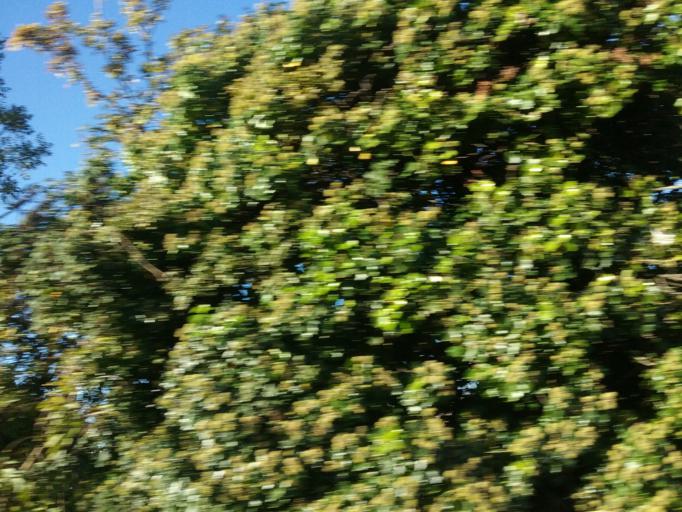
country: IE
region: Leinster
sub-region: Lu
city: Drogheda
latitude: 53.7150
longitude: -6.3663
